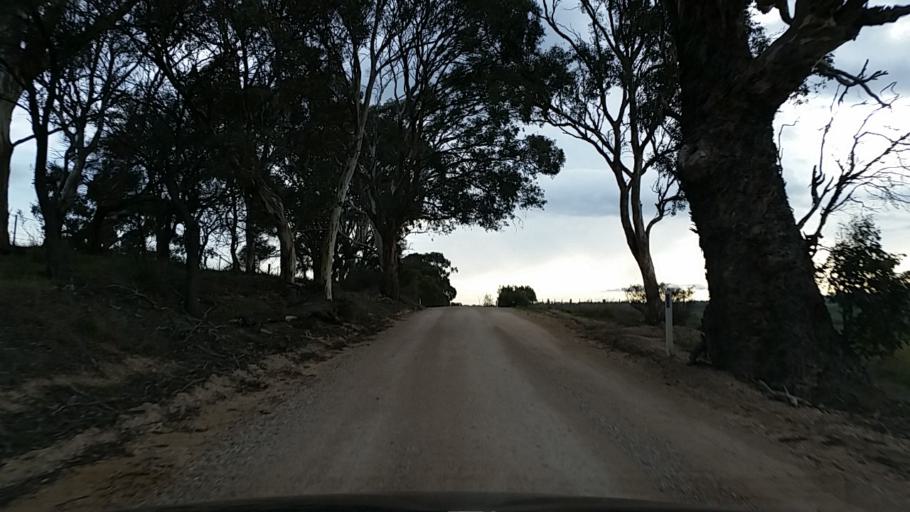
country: AU
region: South Australia
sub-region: Mount Barker
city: Nairne
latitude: -34.9573
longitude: 139.0162
